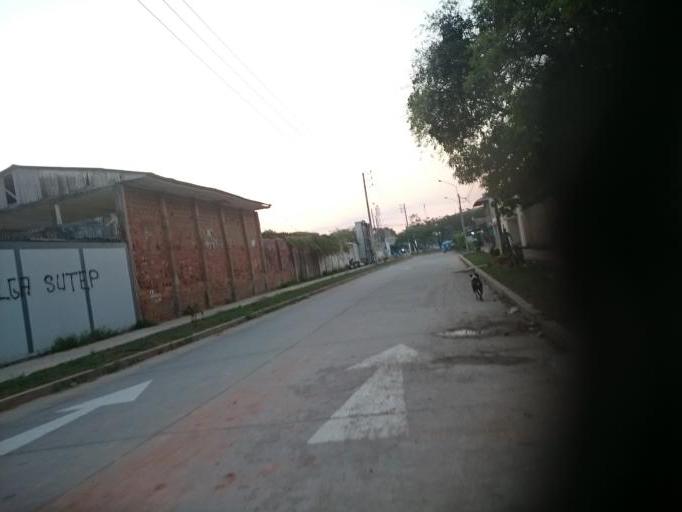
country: PE
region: Ucayali
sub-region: Provincia de Coronel Portillo
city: Pucallpa
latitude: -8.3809
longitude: -74.5365
